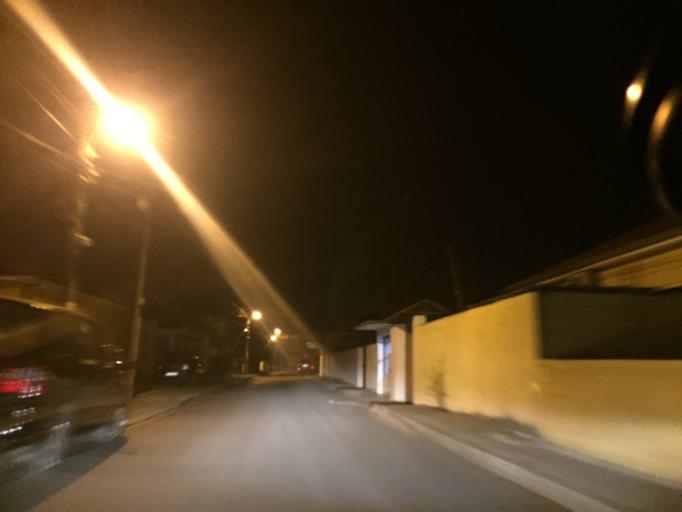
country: AL
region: Shkoder
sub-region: Rrethi i Shkodres
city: Shkoder
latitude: 42.0696
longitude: 19.5037
